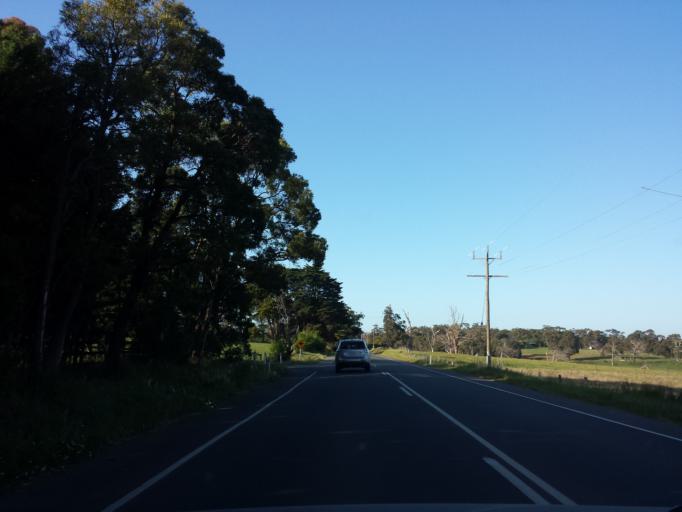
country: AU
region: Victoria
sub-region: Casey
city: Narre Warren North
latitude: -37.9830
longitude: 145.3534
